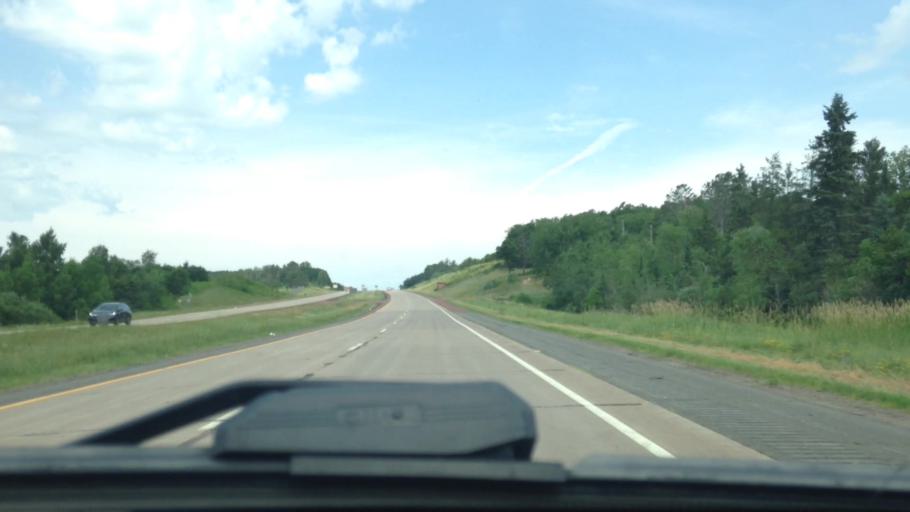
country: US
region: Wisconsin
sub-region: Douglas County
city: Lake Nebagamon
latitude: 46.3265
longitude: -91.8194
